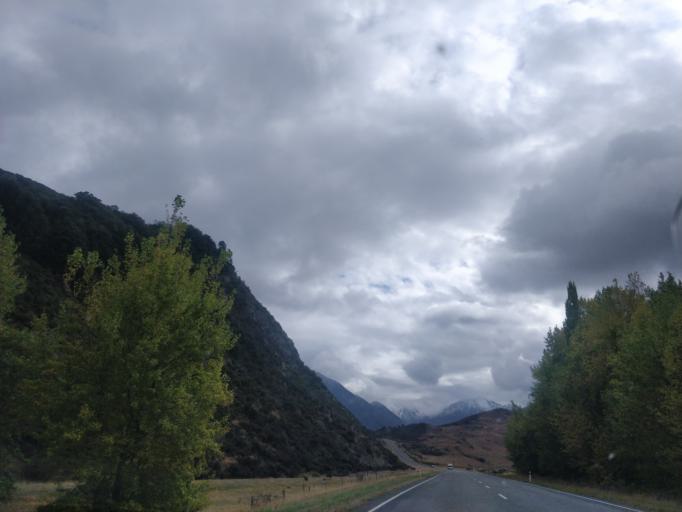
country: NZ
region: Canterbury
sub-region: Waimakariri District
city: Oxford
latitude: -43.0259
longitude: 171.7476
